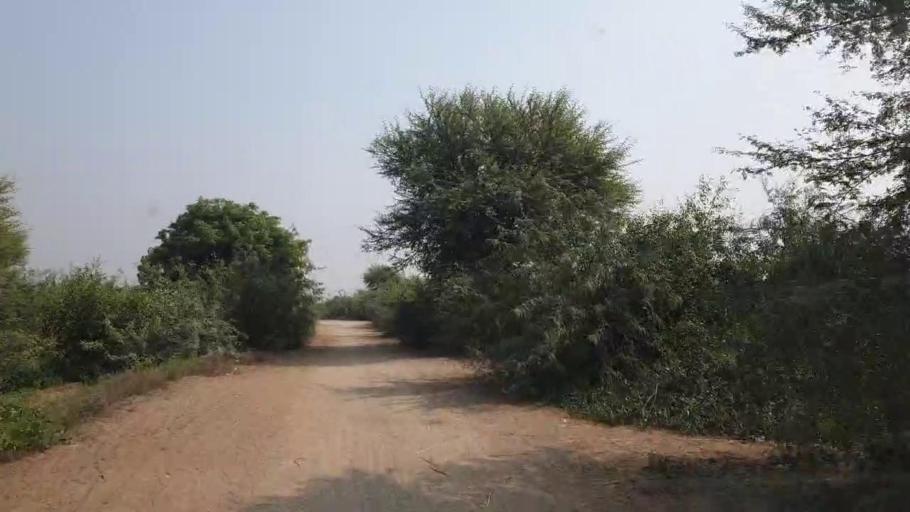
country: PK
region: Sindh
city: Tando Ghulam Ali
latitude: 25.1703
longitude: 68.7298
